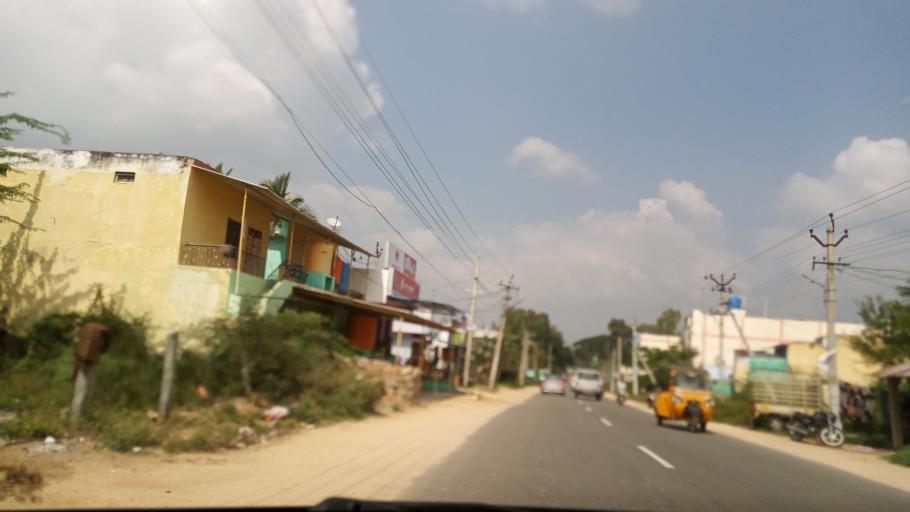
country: IN
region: Andhra Pradesh
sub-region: Chittoor
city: Madanapalle
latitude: 13.6397
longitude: 78.5542
